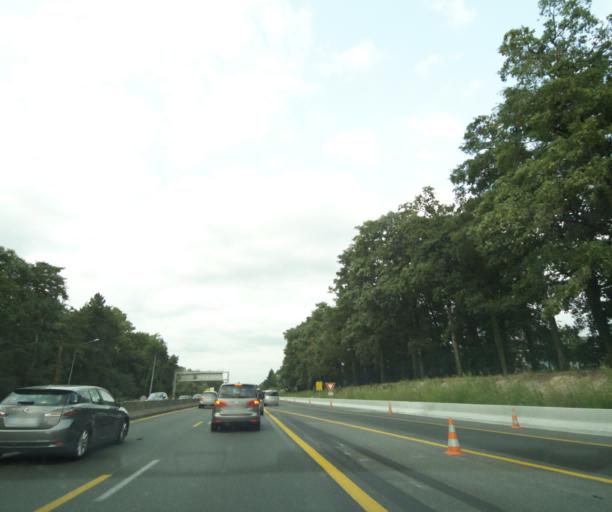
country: FR
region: Centre
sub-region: Departement d'Indre-et-Loire
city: Chambray-les-Tours
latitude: 47.3528
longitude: 0.7062
